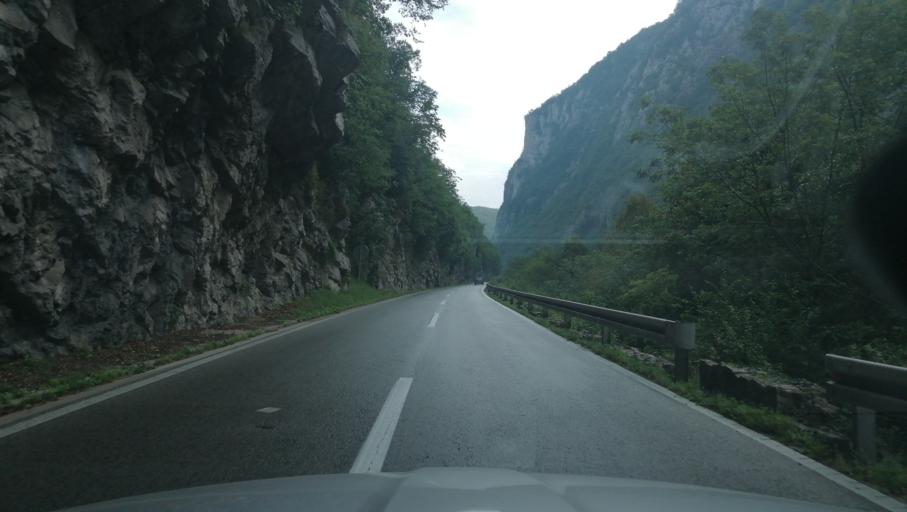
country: BA
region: Republika Srpska
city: Hiseti
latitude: 44.6816
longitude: 17.1712
